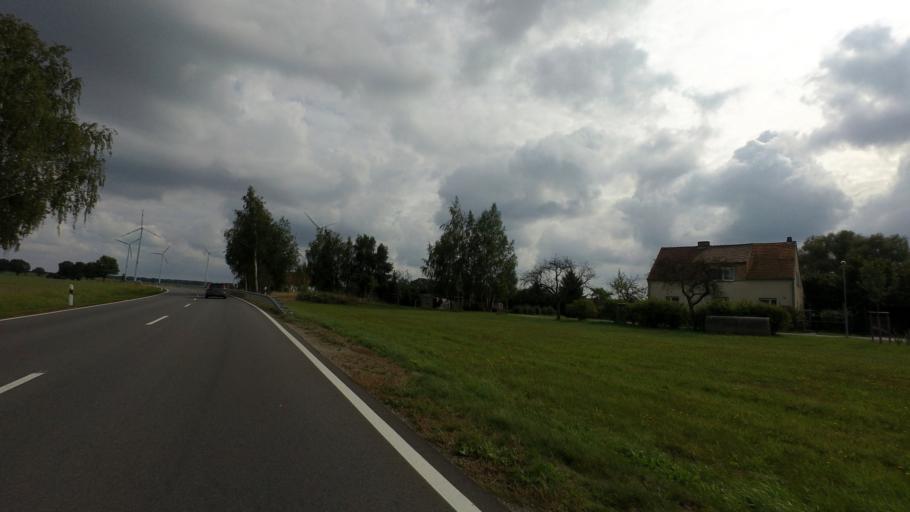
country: DE
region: Brandenburg
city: Sallgast
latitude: 51.6068
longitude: 13.8669
